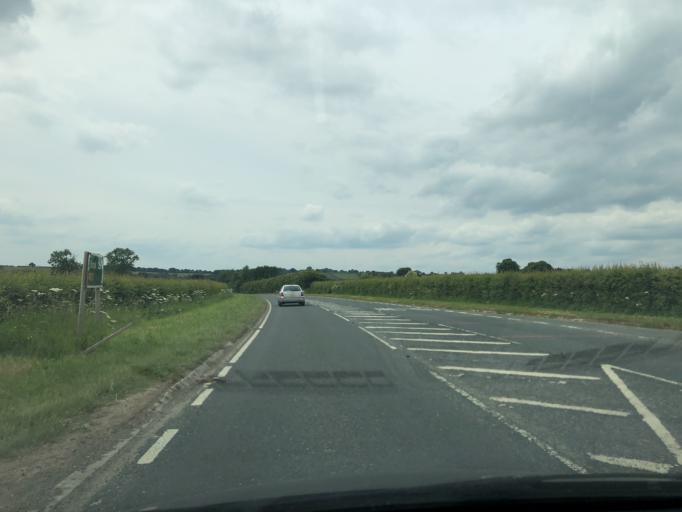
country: GB
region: England
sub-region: North Yorkshire
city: Pickering
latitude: 54.2623
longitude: -0.8163
